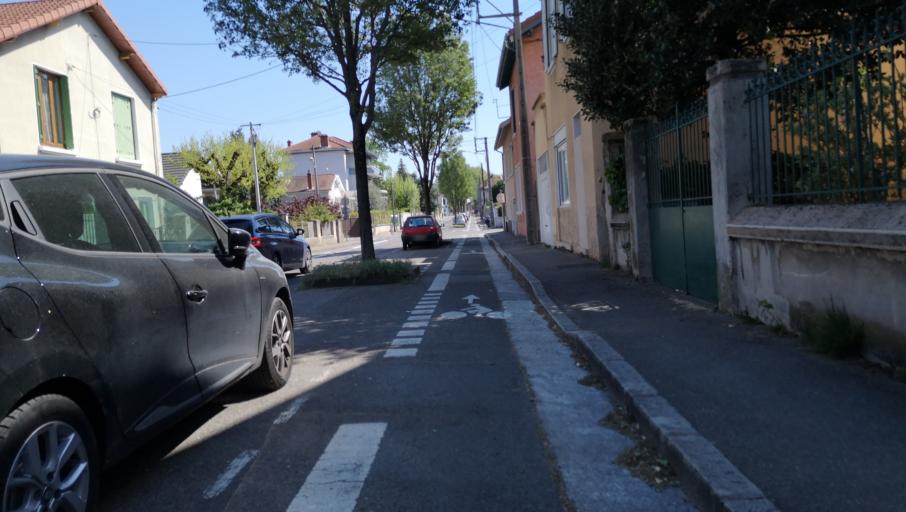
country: FR
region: Rhone-Alpes
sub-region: Departement du Rhone
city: Bron
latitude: 45.7380
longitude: 4.9107
